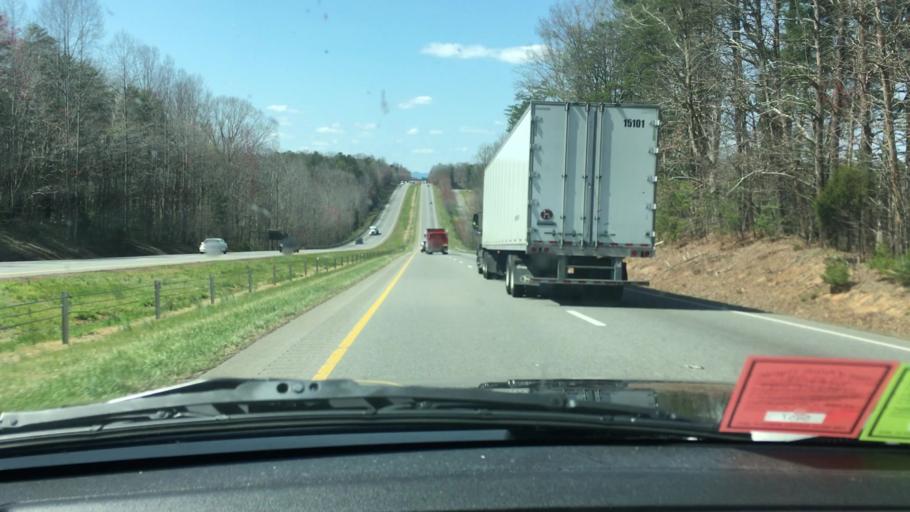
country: US
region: North Carolina
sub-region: Surry County
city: Pilot Mountain
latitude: 36.4233
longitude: -80.5173
